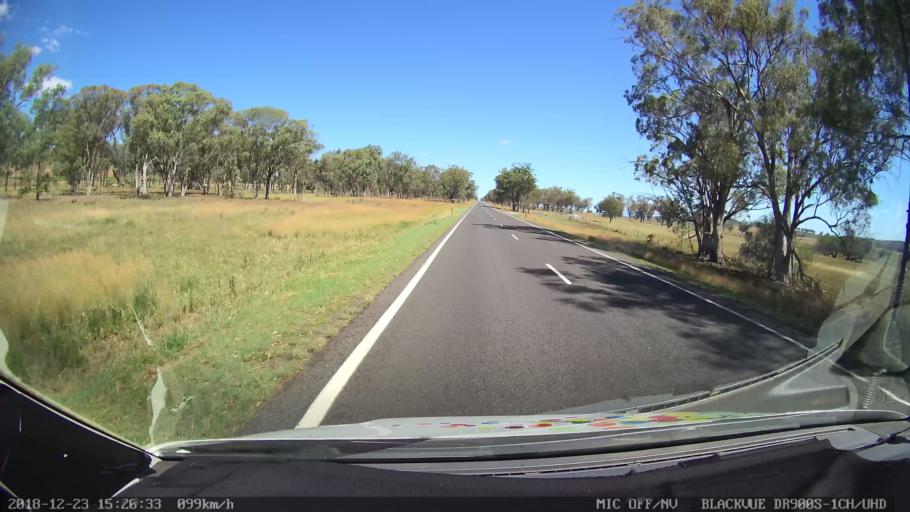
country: AU
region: New South Wales
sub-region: Tamworth Municipality
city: Manilla
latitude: -30.8443
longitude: 150.7905
